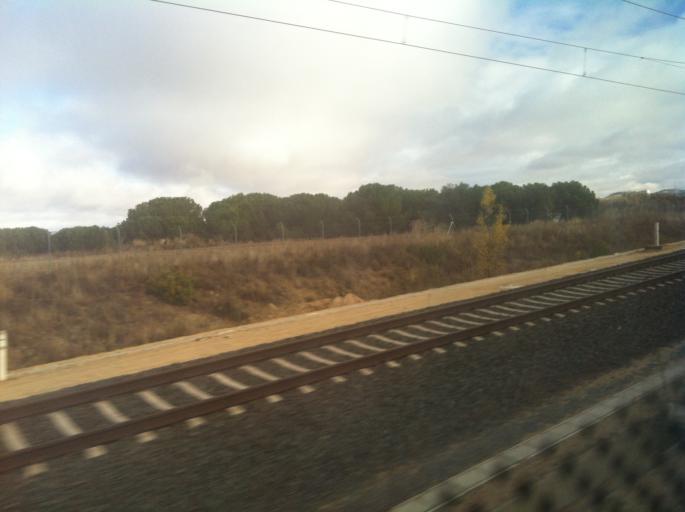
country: ES
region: Castille and Leon
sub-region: Provincia de Burgos
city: Villalbilla de Burgos
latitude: 42.3635
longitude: -3.7434
